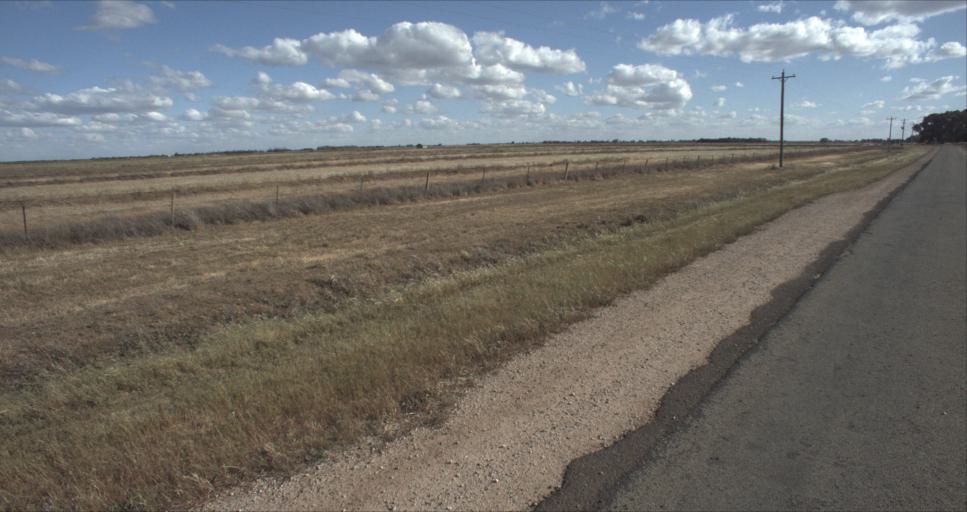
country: AU
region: New South Wales
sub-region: Leeton
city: Leeton
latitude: -34.4566
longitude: 146.2726
